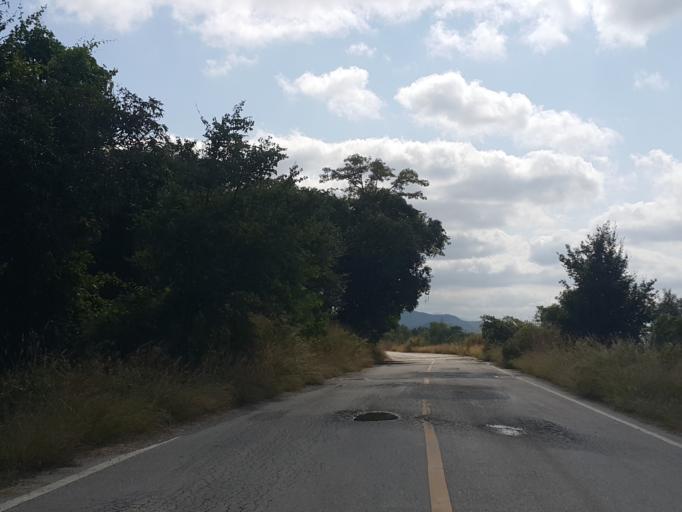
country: TH
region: Lamphun
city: Lamphun
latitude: 18.5536
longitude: 99.0864
